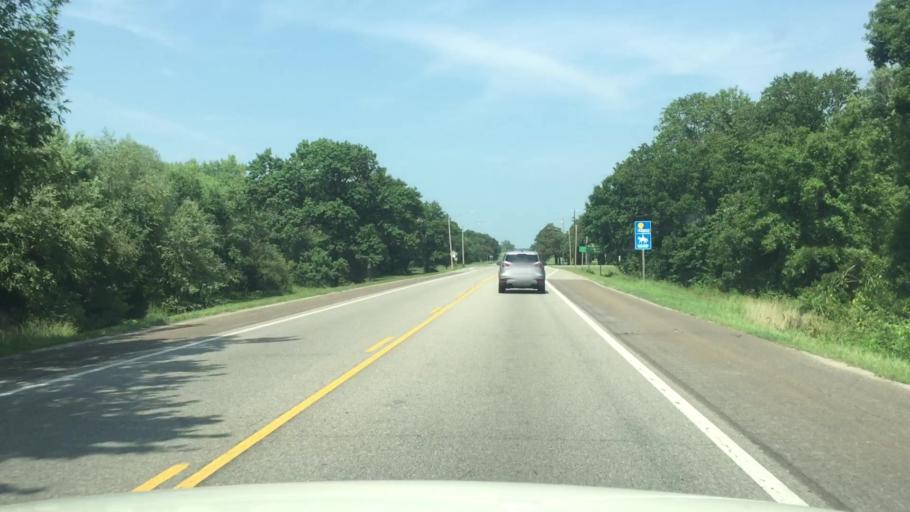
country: US
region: Kansas
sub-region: Crawford County
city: Pittsburg
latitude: 37.4169
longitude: -94.7213
